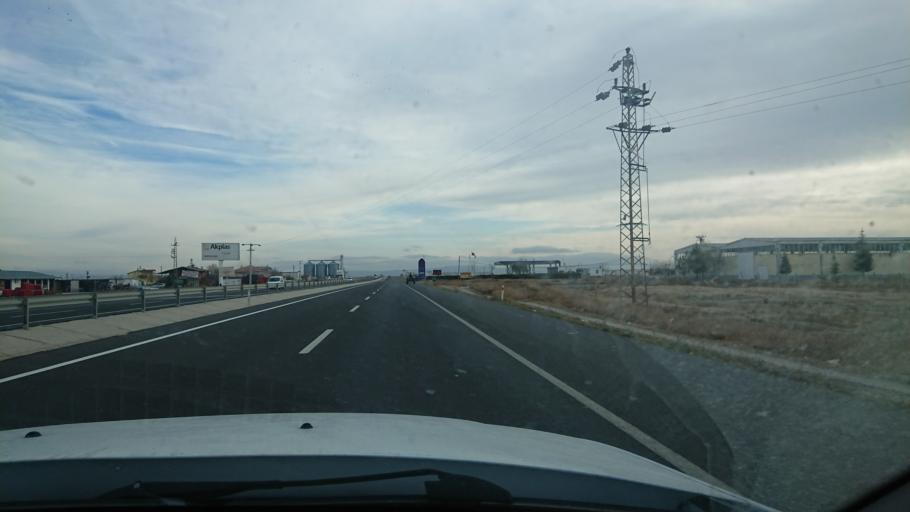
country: TR
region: Aksaray
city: Yesilova
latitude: 38.3260
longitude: 33.8868
